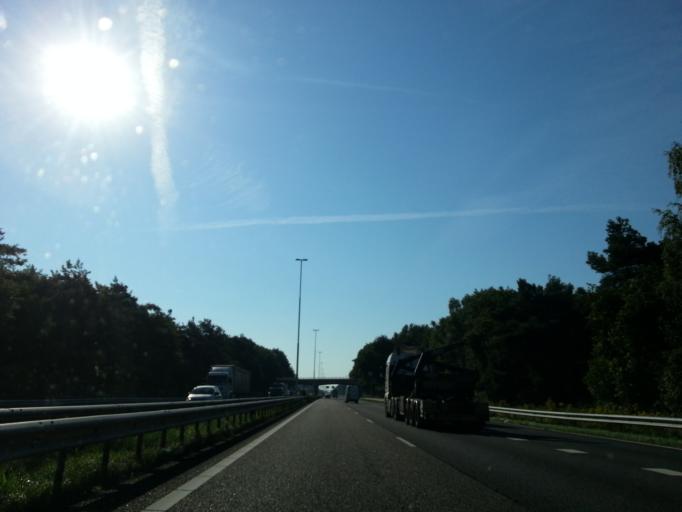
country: NL
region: North Brabant
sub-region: Gemeente Oisterwijk
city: Oisterwijk
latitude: 51.5475
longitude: 5.1456
